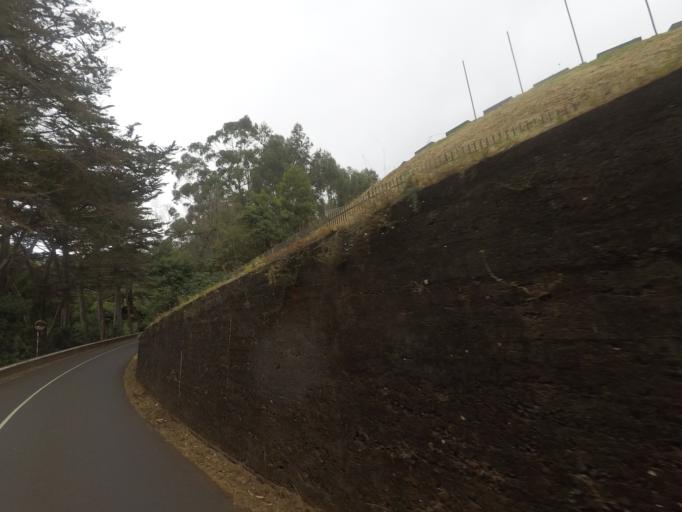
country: PT
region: Madeira
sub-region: Funchal
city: Nossa Senhora do Monte
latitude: 32.6681
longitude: -16.8791
